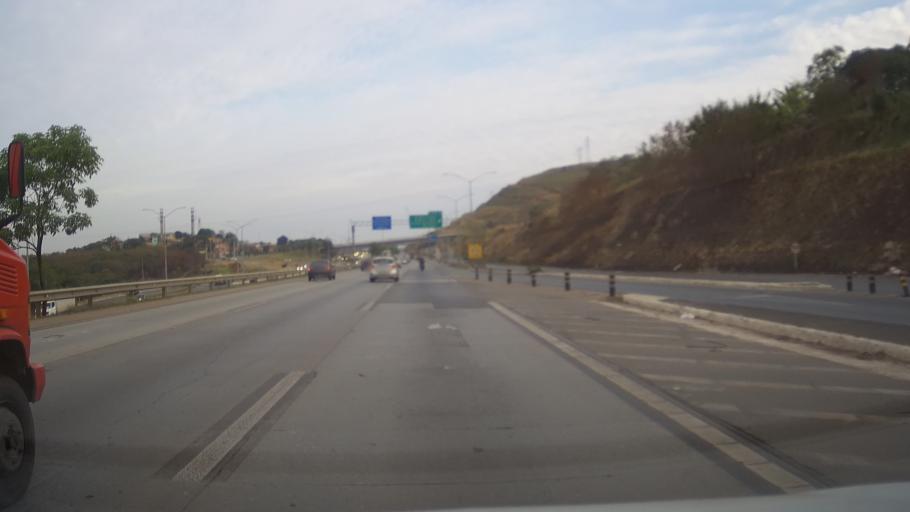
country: BR
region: Minas Gerais
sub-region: Vespasiano
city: Vespasiano
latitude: -19.7836
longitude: -43.9486
